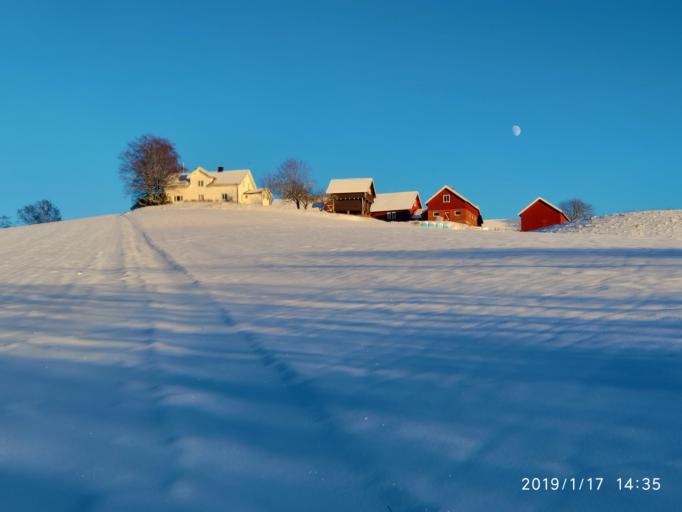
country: NO
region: Akershus
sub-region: Nannestad
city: Teigebyen
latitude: 60.1691
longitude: 11.0157
